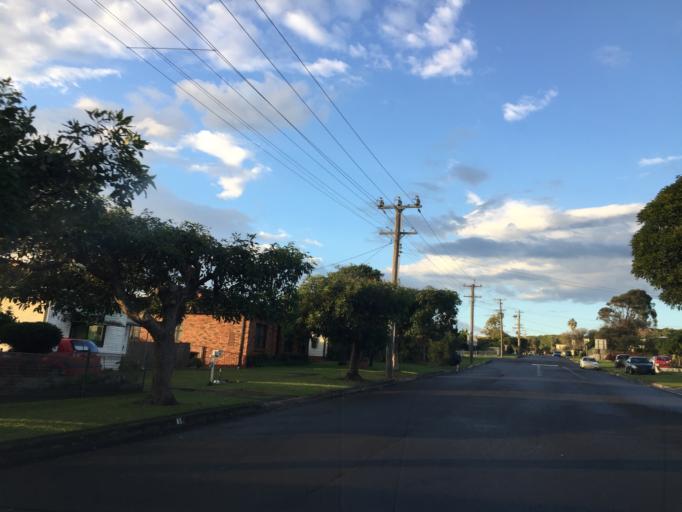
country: AU
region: New South Wales
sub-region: Shellharbour
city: Barrack Heights
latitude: -34.5634
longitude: 150.8540
